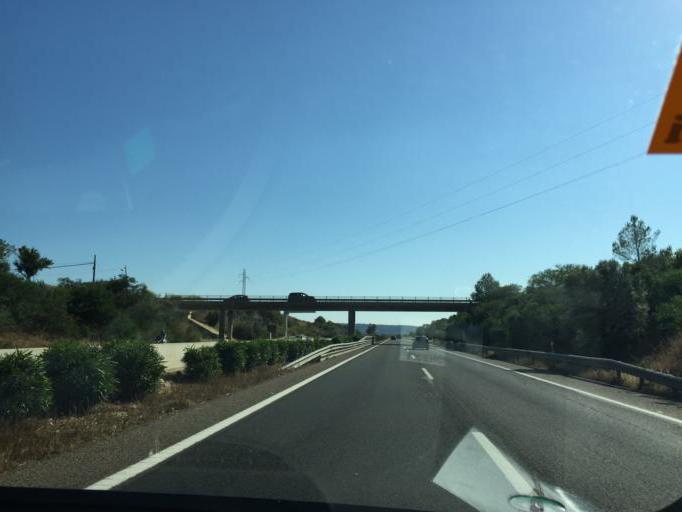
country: ES
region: Balearic Islands
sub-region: Illes Balears
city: Consell
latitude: 39.6655
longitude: 2.8176
